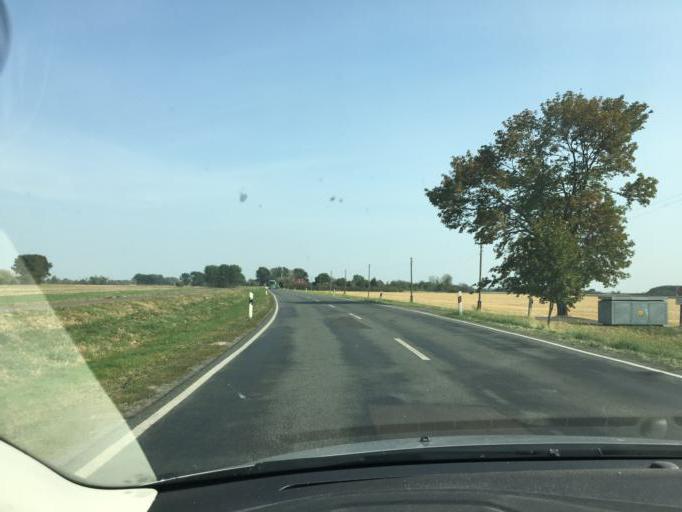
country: DE
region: Saxony-Anhalt
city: Plotzky
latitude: 52.0114
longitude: 11.7818
